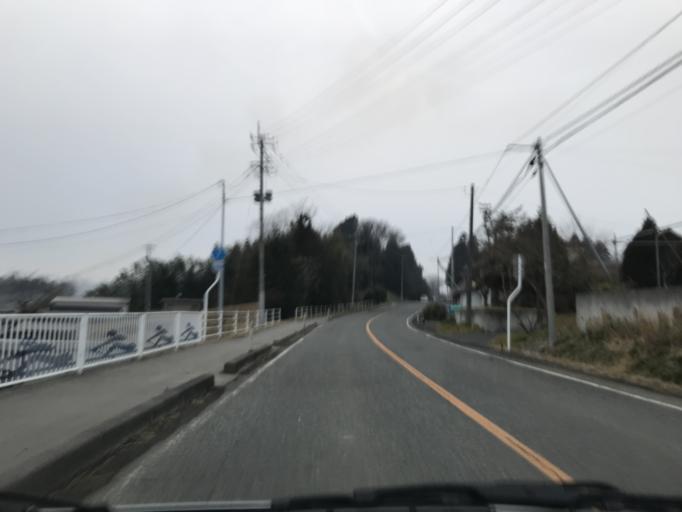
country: JP
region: Miyagi
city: Wakuya
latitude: 38.6782
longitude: 141.1185
